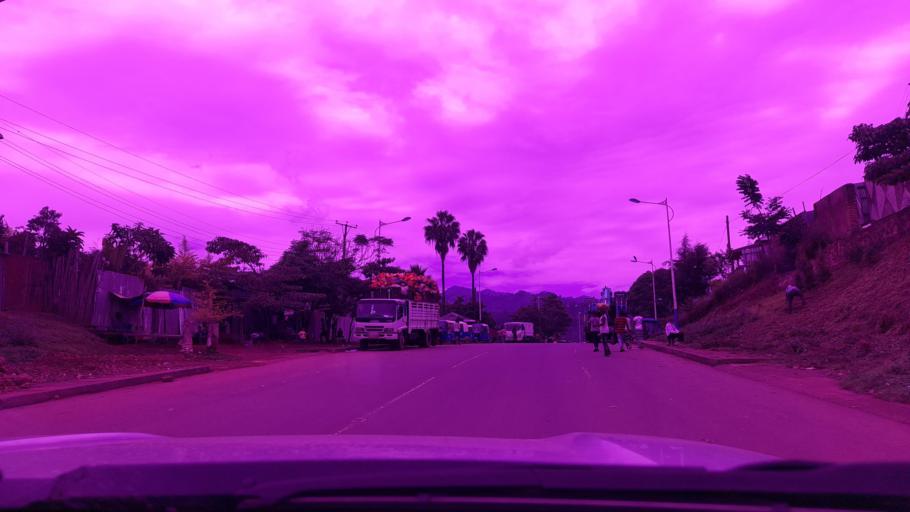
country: ET
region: Southern Nations, Nationalities, and People's Region
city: Mizan Teferi
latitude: 6.9983
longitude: 35.5948
